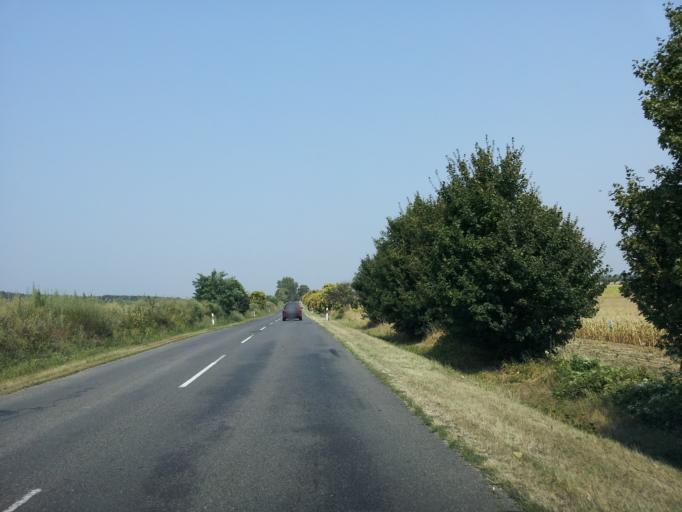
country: HU
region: Gyor-Moson-Sopron
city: Pannonhalma
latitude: 47.4788
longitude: 17.7895
